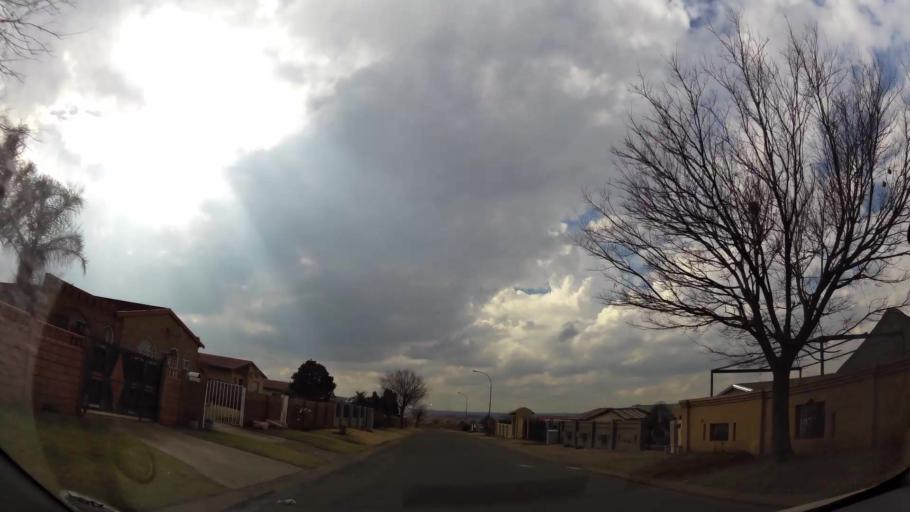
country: ZA
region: Gauteng
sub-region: Ekurhuleni Metropolitan Municipality
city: Germiston
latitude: -26.3905
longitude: 28.1532
